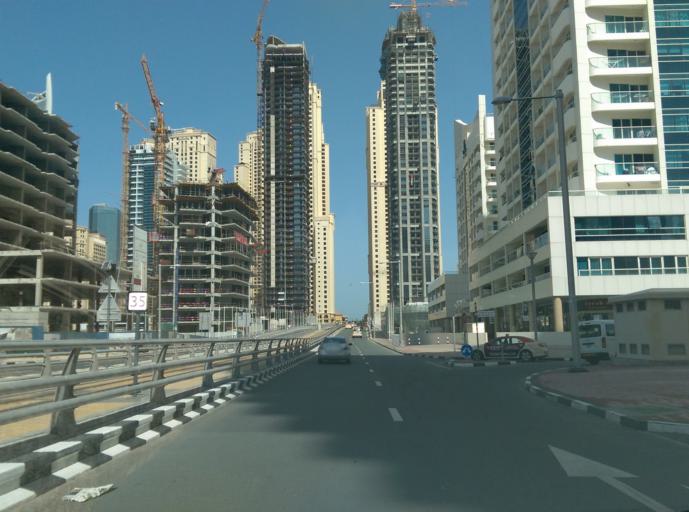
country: AE
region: Dubai
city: Dubai
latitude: 25.0784
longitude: 55.1428
